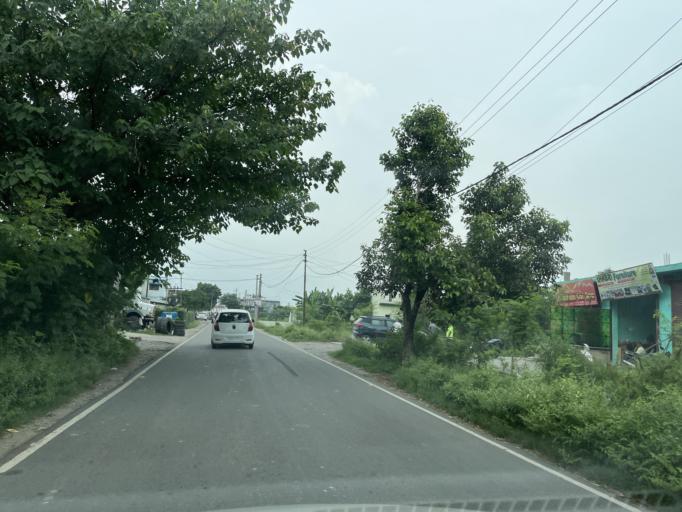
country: IN
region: Uttarakhand
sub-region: Naini Tal
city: Haldwani
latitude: 29.1956
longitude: 79.4847
